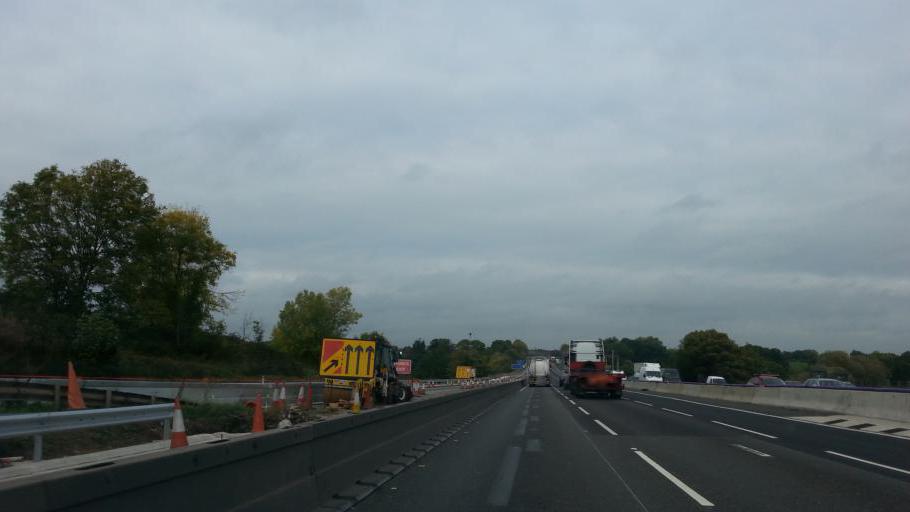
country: GB
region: England
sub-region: Cheshire East
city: Holmes Chapel
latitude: 53.2035
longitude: -2.3879
